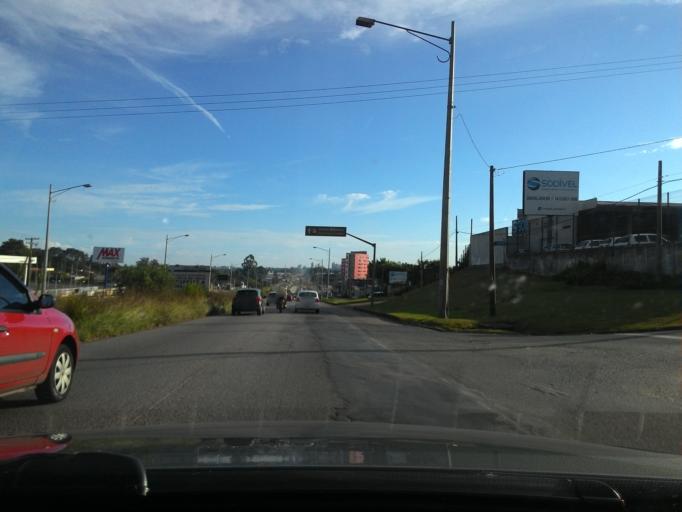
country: BR
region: Parana
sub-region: Pinhais
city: Pinhais
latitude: -25.4007
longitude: -49.2163
